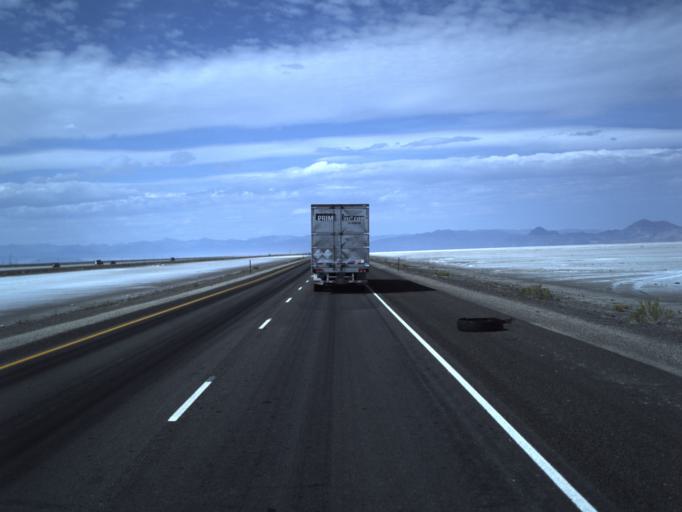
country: US
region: Utah
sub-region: Tooele County
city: Wendover
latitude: 40.7356
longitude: -113.6679
